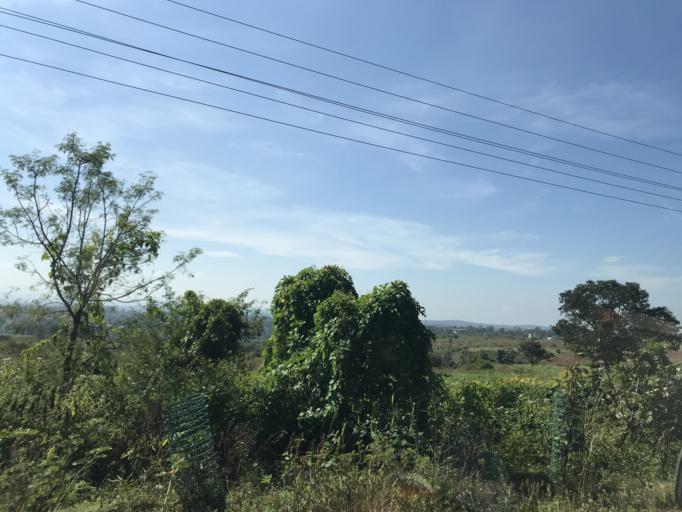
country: IN
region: Karnataka
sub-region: Mysore
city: Heggadadevankote
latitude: 12.0153
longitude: 76.2714
